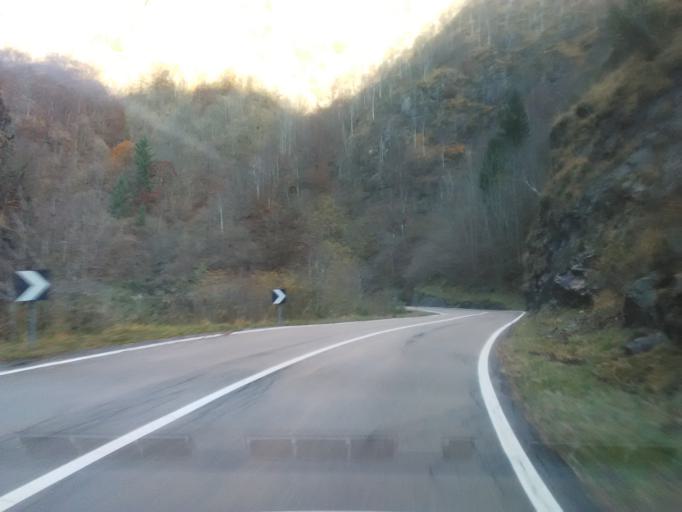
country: IT
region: Piedmont
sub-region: Provincia di Vercelli
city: Cervatto
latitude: 45.8802
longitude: 8.1785
